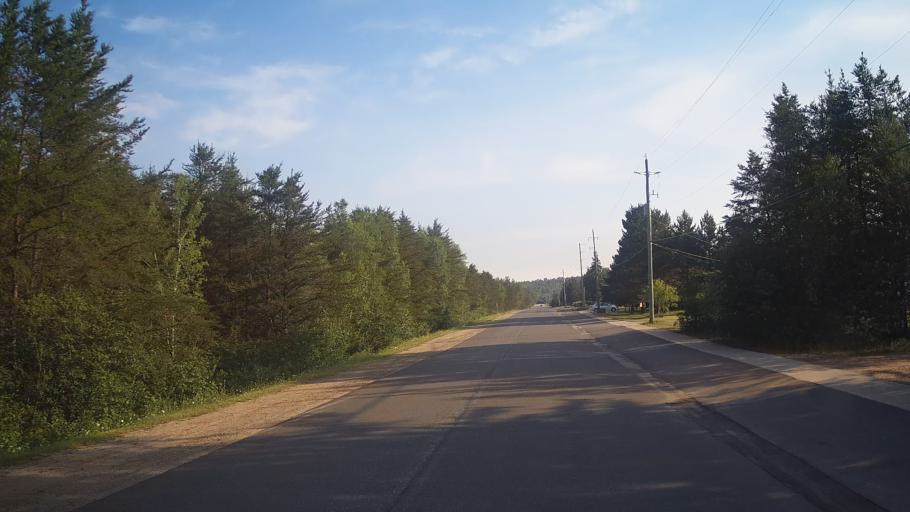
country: CA
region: Ontario
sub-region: Rainy River District
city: Atikokan
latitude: 49.4086
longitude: -91.6663
